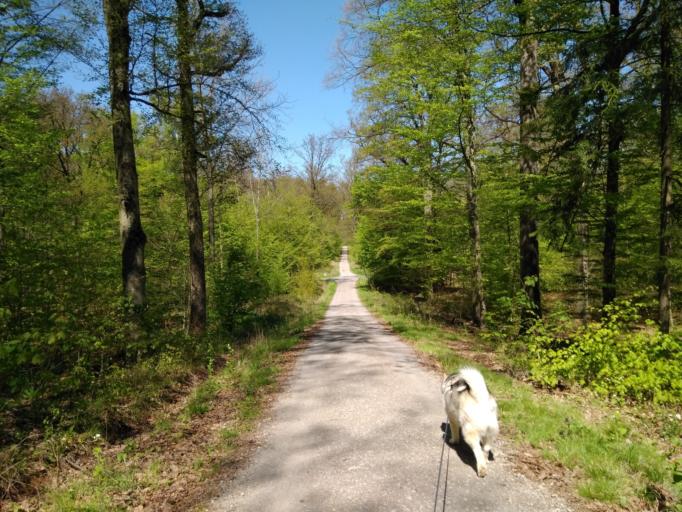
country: DE
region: Baden-Wuerttemberg
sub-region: Regierungsbezirk Stuttgart
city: Gerlingen
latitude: 48.7940
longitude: 9.0873
